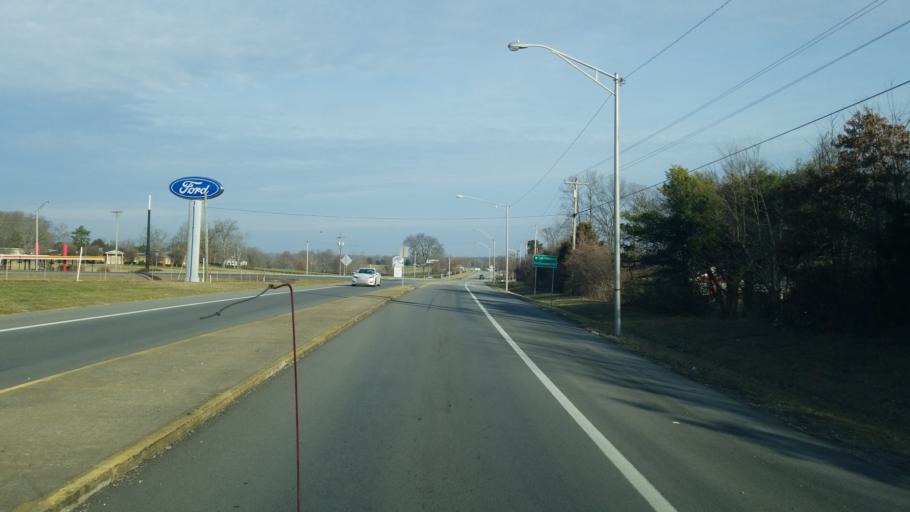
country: US
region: Kentucky
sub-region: Russell County
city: Russell Springs
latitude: 37.0678
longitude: -85.0715
